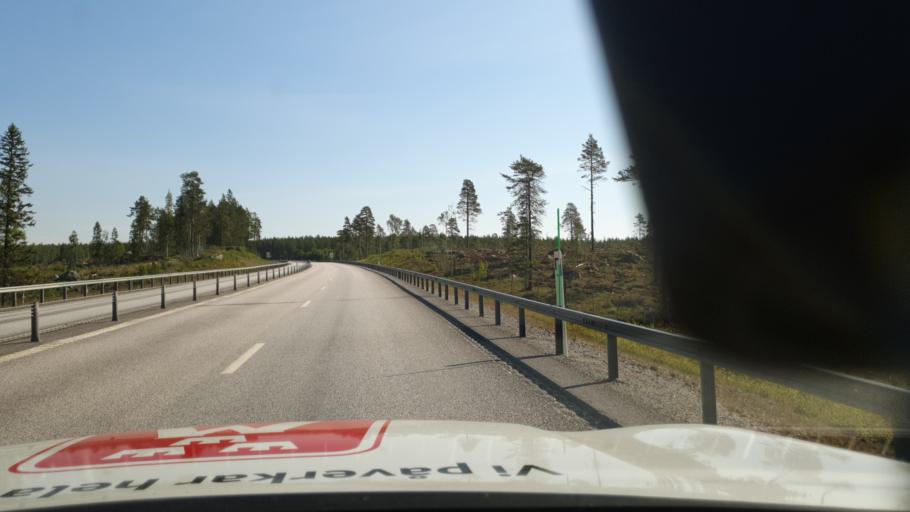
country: SE
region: Vaesterbotten
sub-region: Umea Kommun
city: Saevar
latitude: 63.9281
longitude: 20.6322
